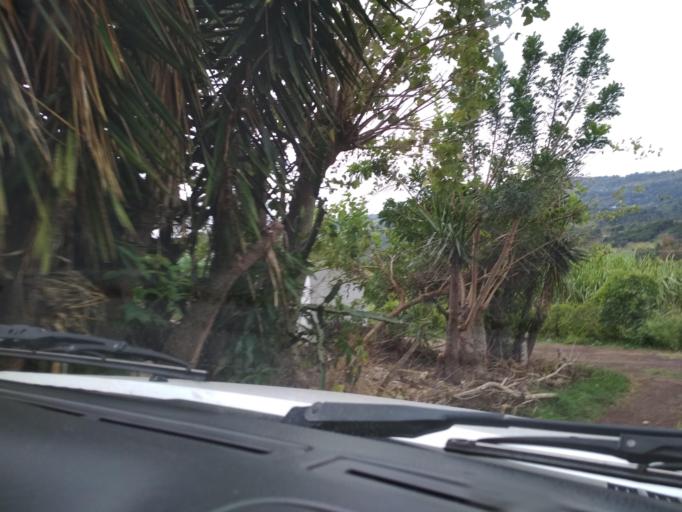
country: MX
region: Veracruz
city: El Castillo
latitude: 19.5830
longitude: -96.8400
